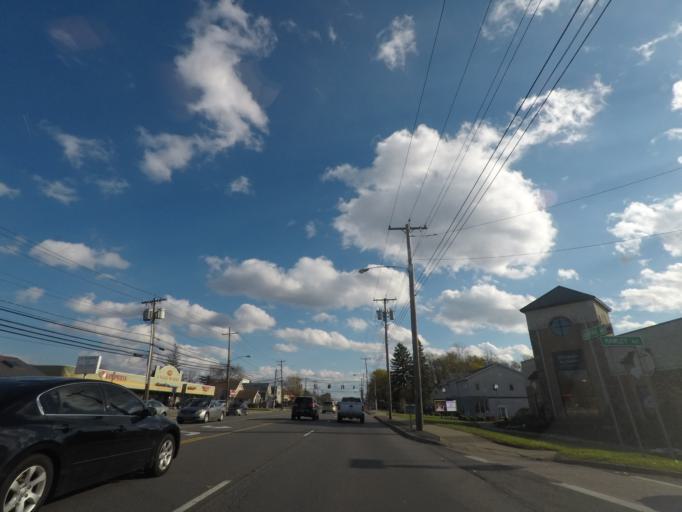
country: US
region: New York
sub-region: Albany County
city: Colonie
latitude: 42.7149
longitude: -73.8298
